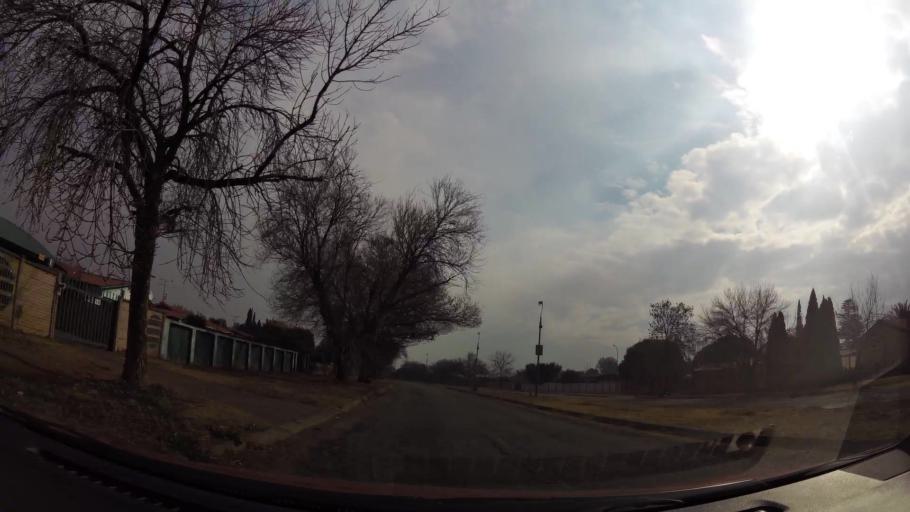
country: ZA
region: Gauteng
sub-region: Sedibeng District Municipality
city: Vanderbijlpark
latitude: -26.6898
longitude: 27.8461
